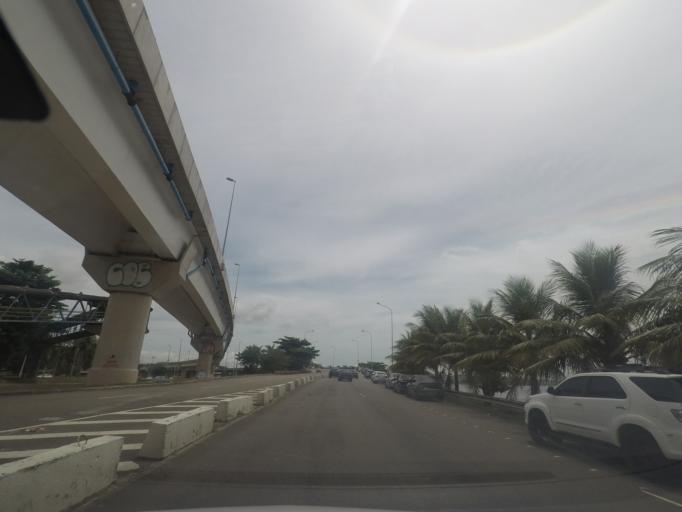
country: BR
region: Rio de Janeiro
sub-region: Rio De Janeiro
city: Rio de Janeiro
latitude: -22.8258
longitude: -43.2325
